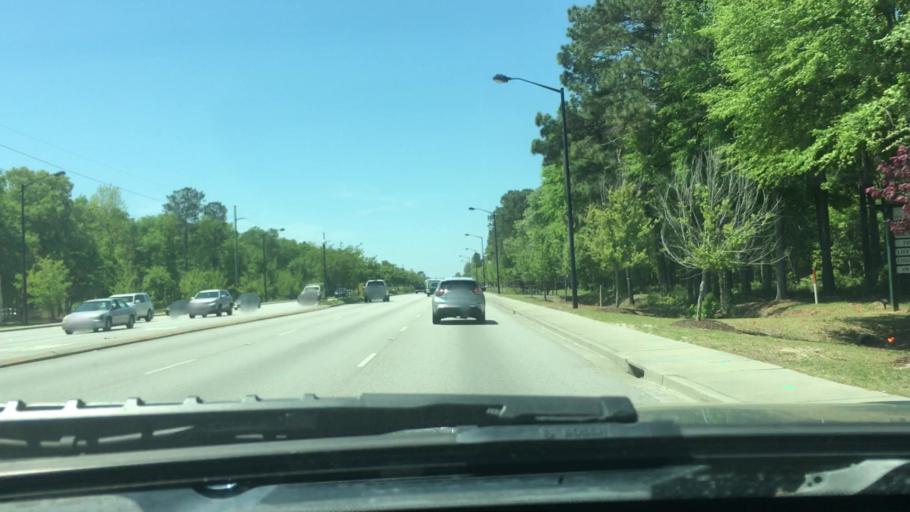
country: US
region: South Carolina
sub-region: Charleston County
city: Isle of Palms
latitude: 32.8646
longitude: -79.7872
